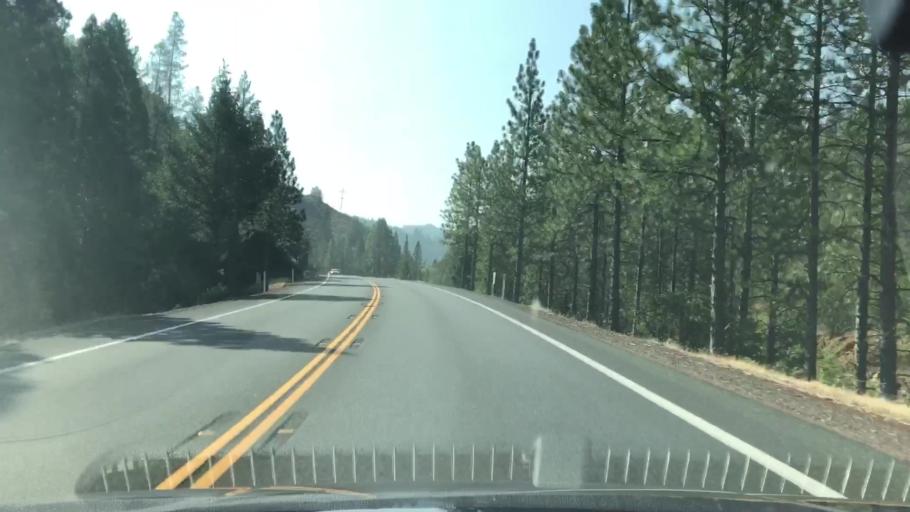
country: US
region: California
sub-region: Lake County
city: Middletown
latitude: 38.6898
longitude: -122.5971
